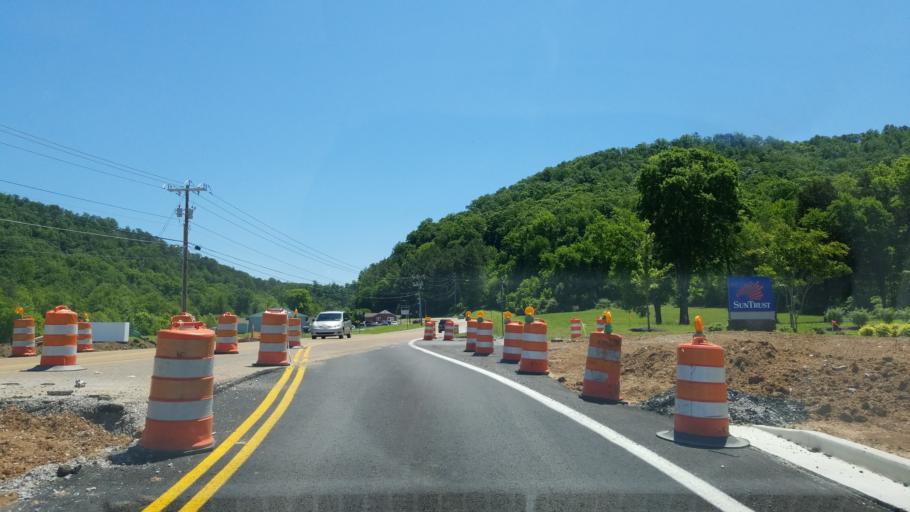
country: US
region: Tennessee
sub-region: Hamilton County
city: Collegedale
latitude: 35.0587
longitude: -85.0646
